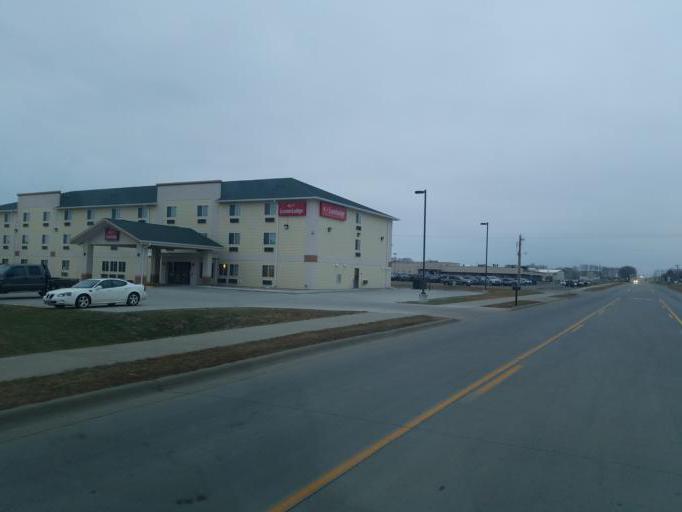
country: US
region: South Dakota
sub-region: Yankton County
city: Yankton
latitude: 42.8944
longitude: -97.4001
